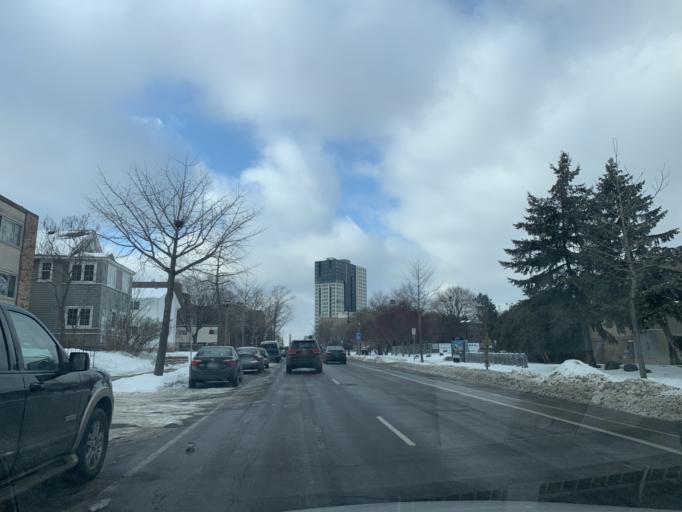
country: US
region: Minnesota
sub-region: Hennepin County
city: Minneapolis
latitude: 44.9863
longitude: -93.2503
